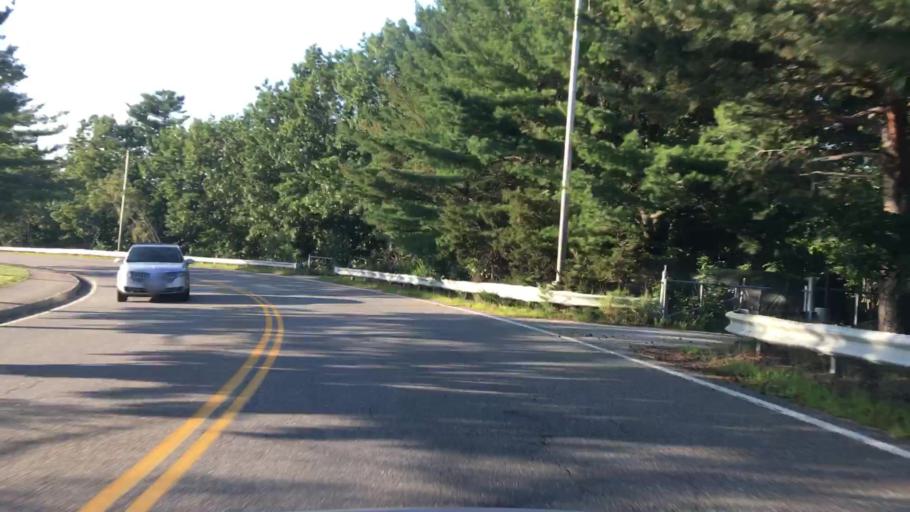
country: US
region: Maine
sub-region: Cumberland County
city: South Portland Gardens
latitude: 43.6327
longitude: -70.3299
